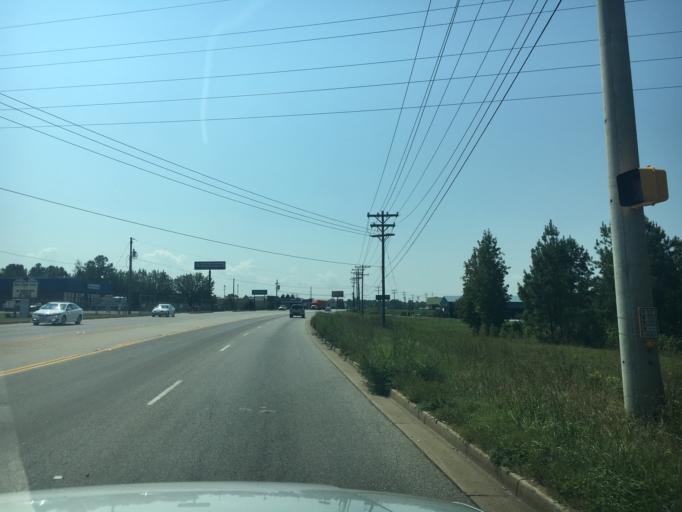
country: US
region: South Carolina
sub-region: Anderson County
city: Centerville
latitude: 34.5483
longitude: -82.6966
